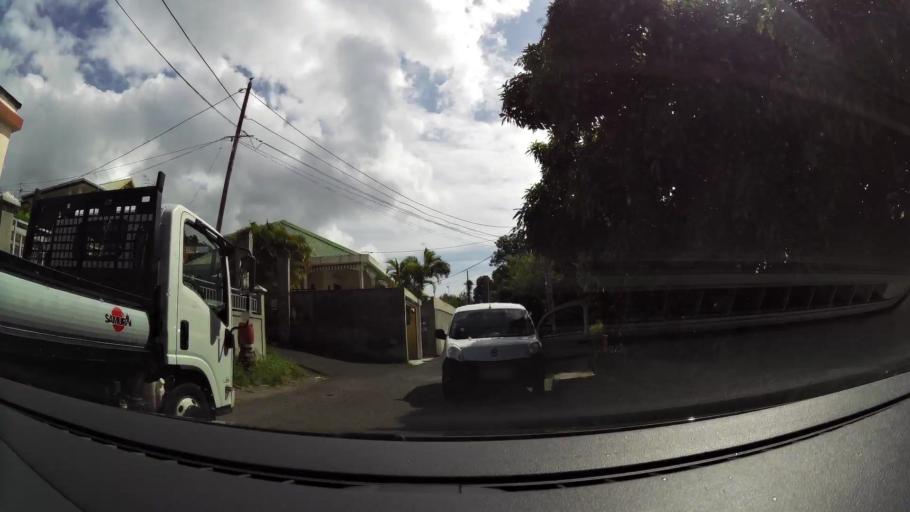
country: GP
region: Guadeloupe
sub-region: Guadeloupe
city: Basse-Terre
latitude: 16.0048
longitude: -61.7346
